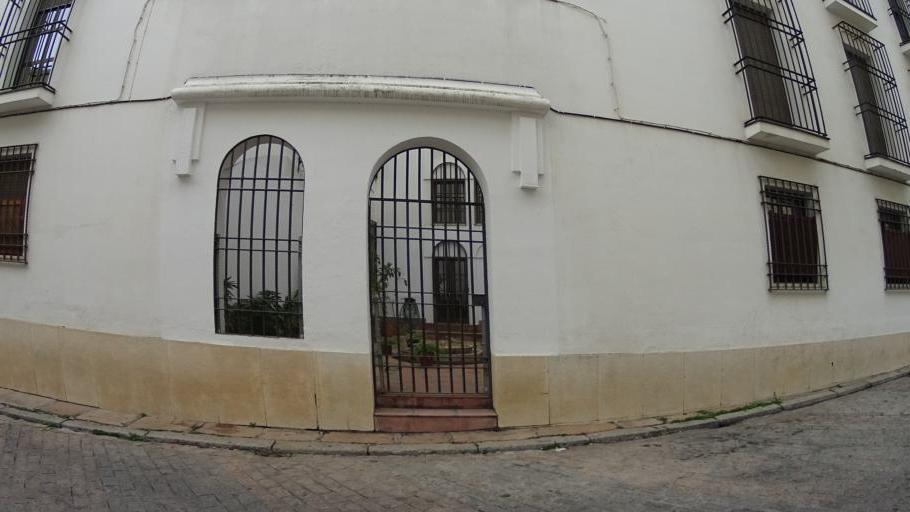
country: ES
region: Andalusia
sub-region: Province of Cordoba
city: Cordoba
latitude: 37.8824
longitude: -4.7844
